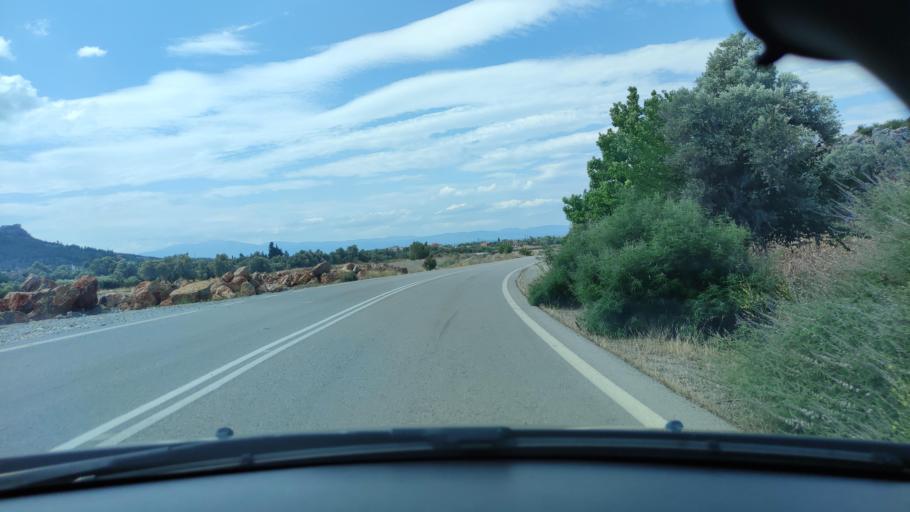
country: GR
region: Central Greece
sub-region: Nomos Evvoias
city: Afration
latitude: 38.4569
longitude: 23.6817
